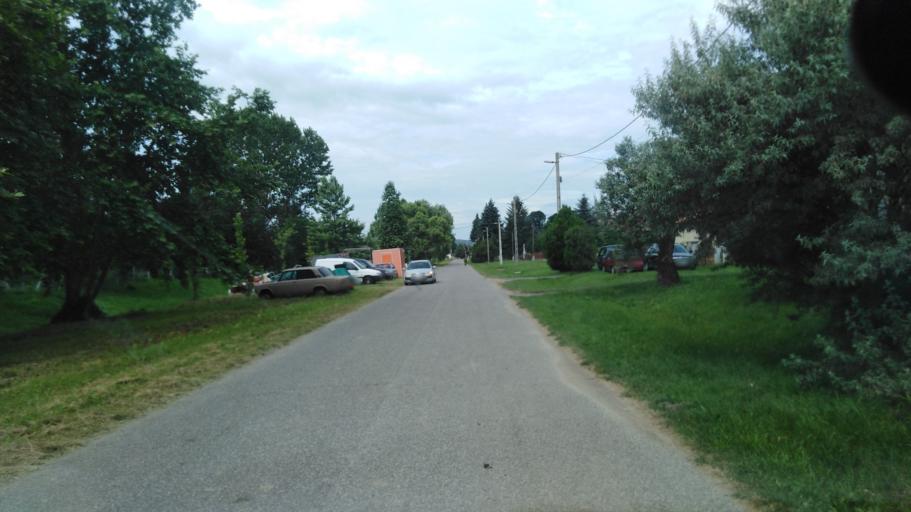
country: HU
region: Nograd
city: Karancskeszi
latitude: 48.2348
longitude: 19.6331
